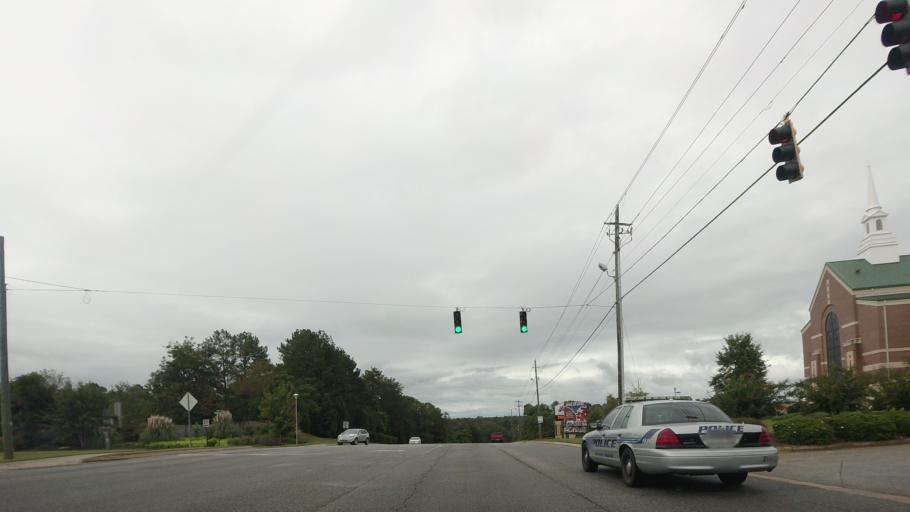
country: US
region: Georgia
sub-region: Houston County
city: Warner Robins
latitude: 32.5791
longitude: -83.6238
